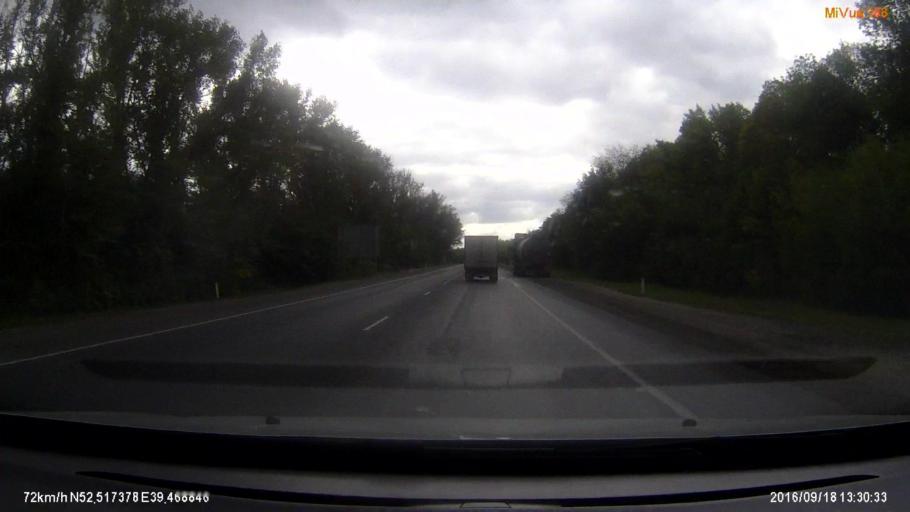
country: RU
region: Lipetsk
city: Borinskoye
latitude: 52.4683
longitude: 39.4173
